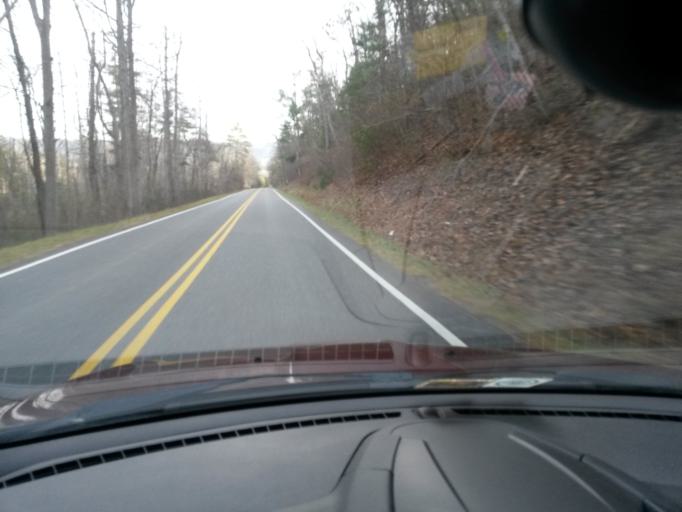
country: US
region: Virginia
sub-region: Alleghany County
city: Clifton Forge
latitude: 37.8744
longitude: -79.7458
